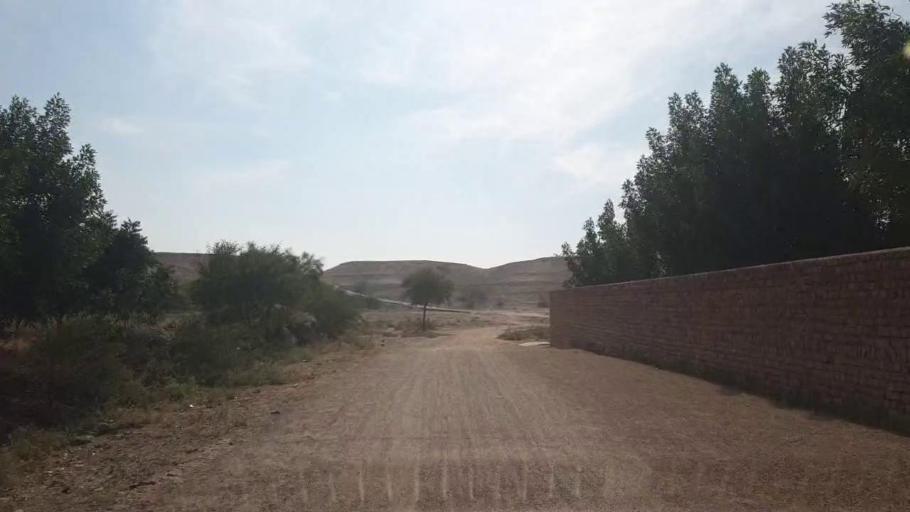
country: PK
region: Sindh
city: Hala
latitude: 25.7395
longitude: 68.2938
